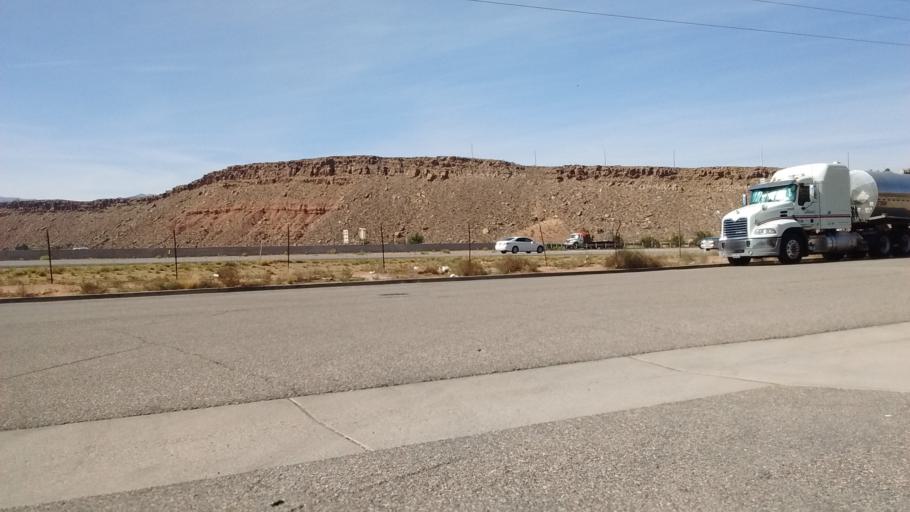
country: US
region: Utah
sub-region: Washington County
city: Saint George
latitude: 37.0626
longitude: -113.5826
